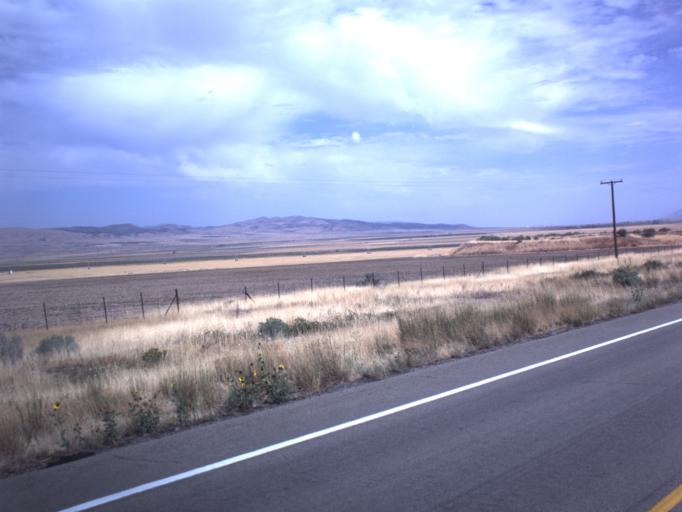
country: US
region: Utah
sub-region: Juab County
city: Nephi
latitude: 39.4665
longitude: -111.8990
